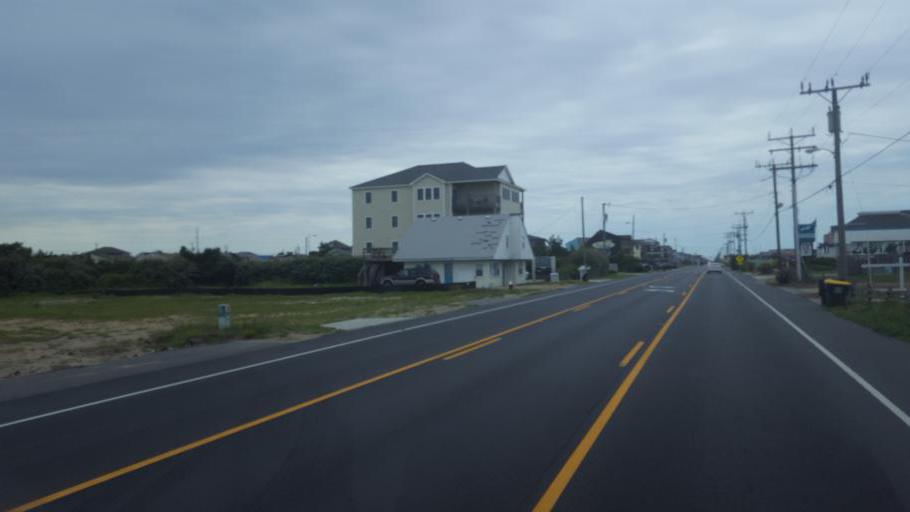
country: US
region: North Carolina
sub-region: Dare County
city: Nags Head
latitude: 35.9955
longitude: -75.6462
